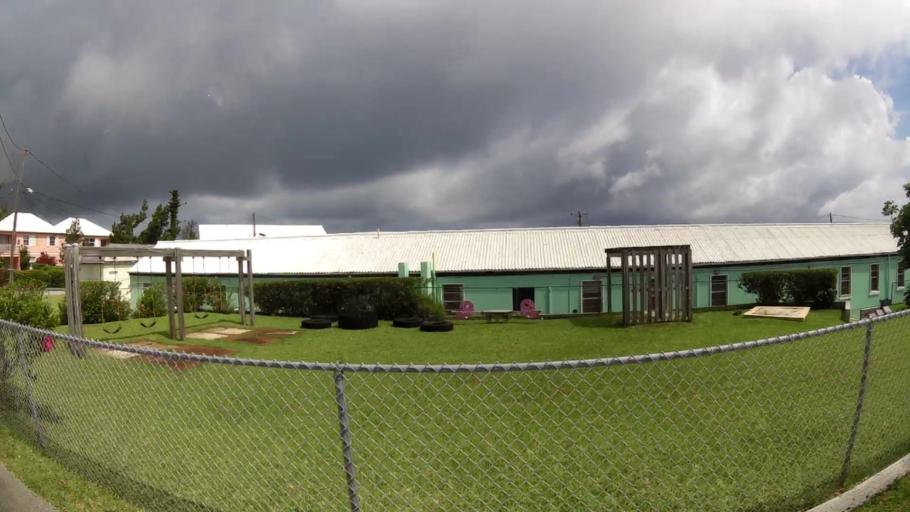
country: BM
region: Saint George
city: Saint George
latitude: 32.3677
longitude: -64.6492
